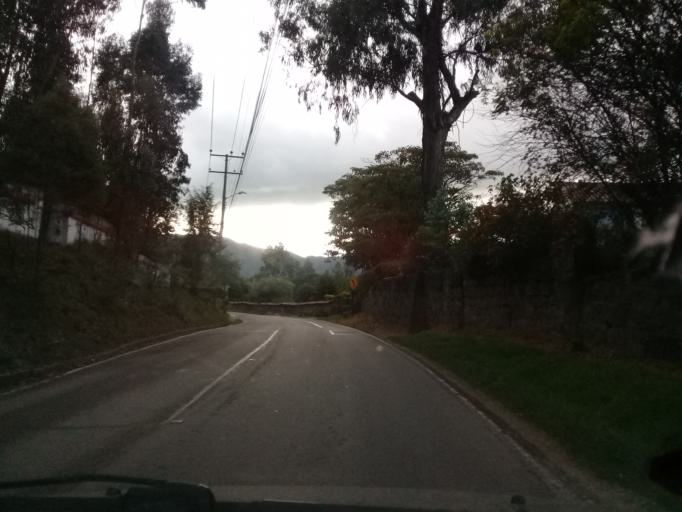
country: CO
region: Cundinamarca
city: Tabio
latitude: 4.9262
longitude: -74.0761
